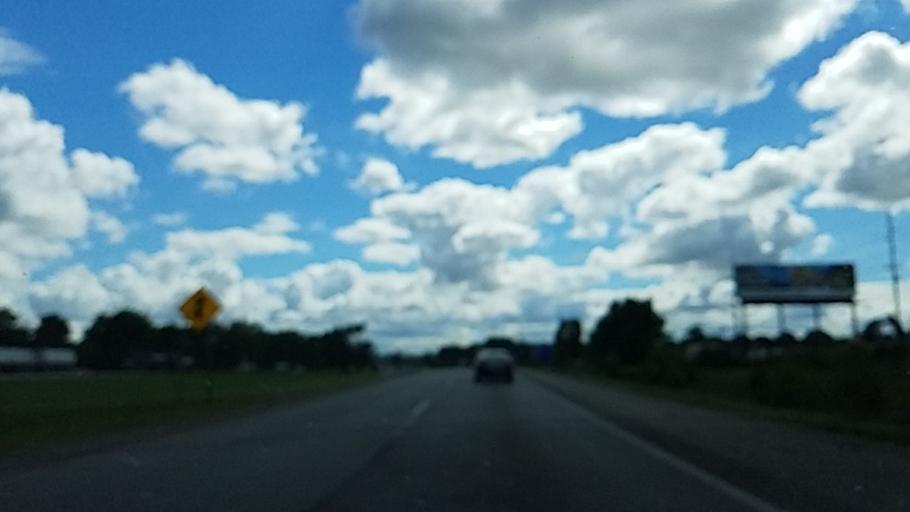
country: US
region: Michigan
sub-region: Livingston County
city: Brighton
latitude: 42.5171
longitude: -83.7581
